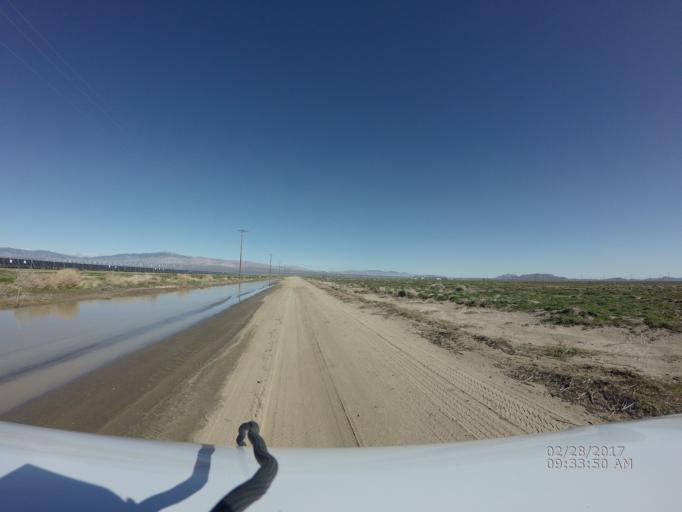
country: US
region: California
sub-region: Los Angeles County
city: Green Valley
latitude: 34.8142
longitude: -118.3614
